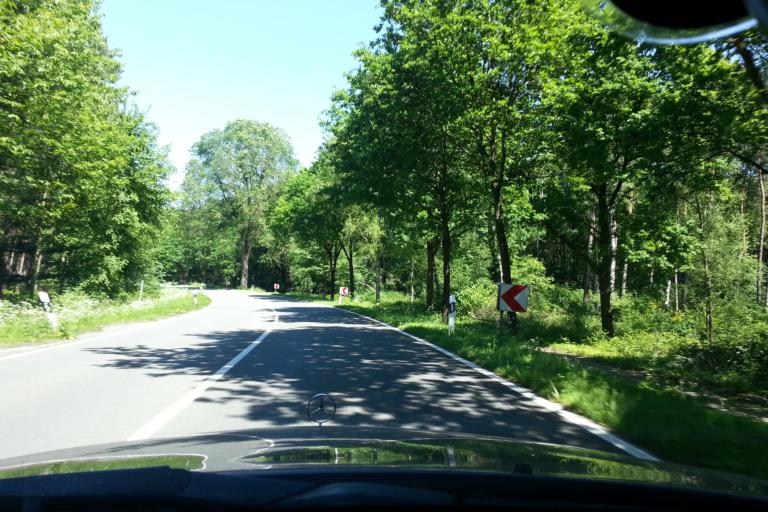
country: DE
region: North Rhine-Westphalia
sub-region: Regierungsbezirk Munster
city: Haltern
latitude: 51.7065
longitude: 7.1939
